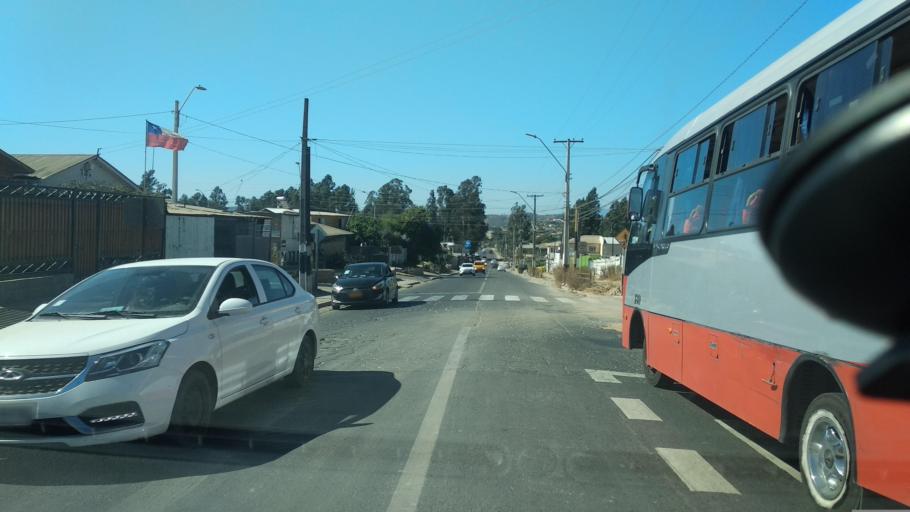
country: CL
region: Valparaiso
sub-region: Provincia de Marga Marga
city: Villa Alemana
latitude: -33.0662
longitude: -71.3712
